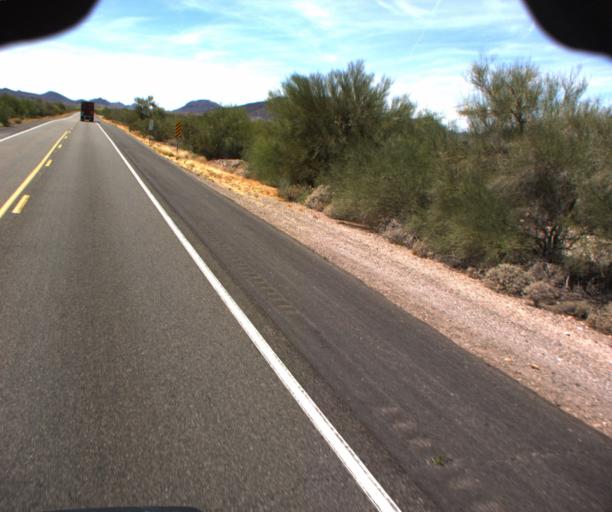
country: US
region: Arizona
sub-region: La Paz County
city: Quartzsite
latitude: 33.6757
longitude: -113.9607
